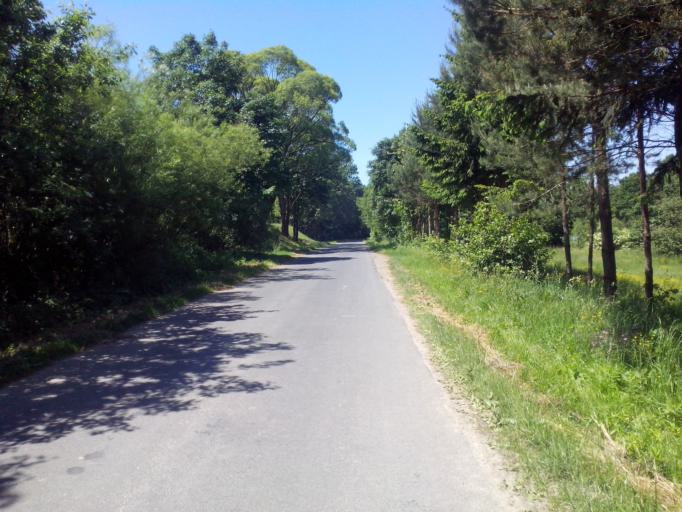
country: PL
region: Subcarpathian Voivodeship
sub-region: Powiat krosnienski
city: Wojaszowka
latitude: 49.7969
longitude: 21.7057
